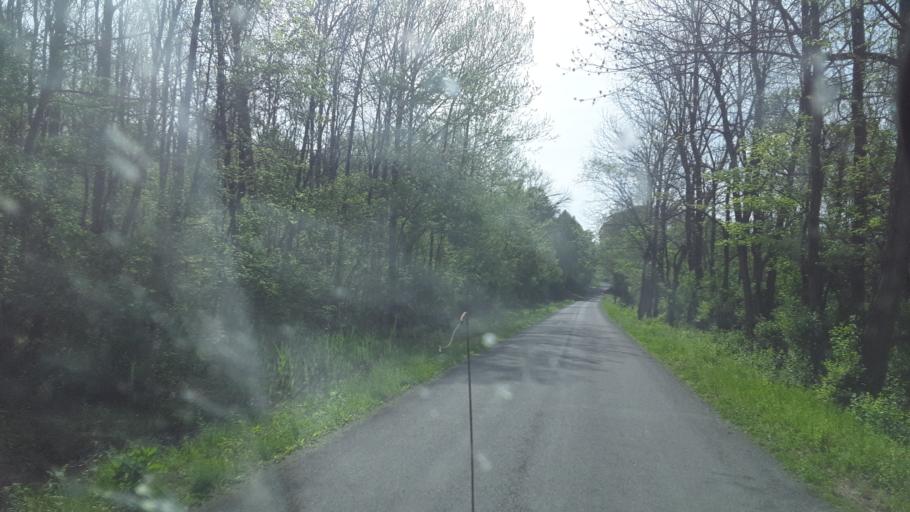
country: US
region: Illinois
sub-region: Jackson County
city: Carbondale
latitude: 37.6808
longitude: -89.2880
